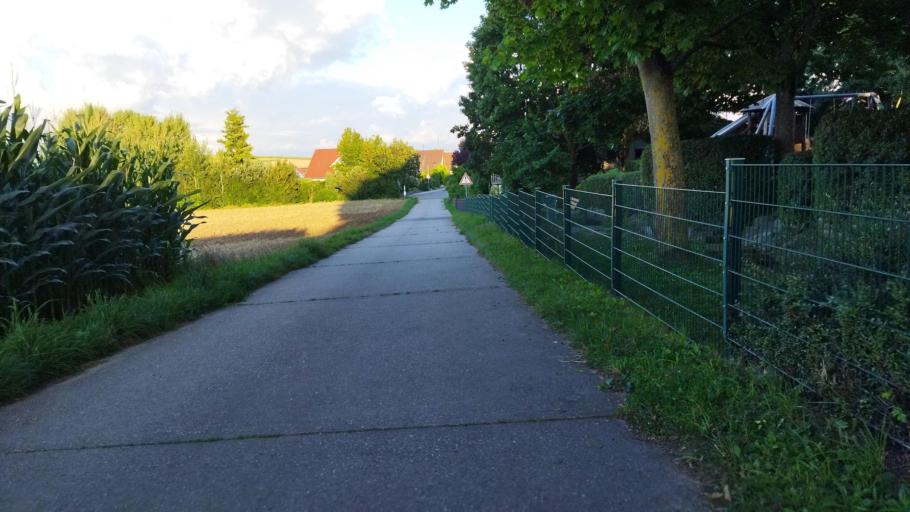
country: DE
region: Baden-Wuerttemberg
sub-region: Regierungsbezirk Stuttgart
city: Brackenheim
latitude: 49.0886
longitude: 9.0726
